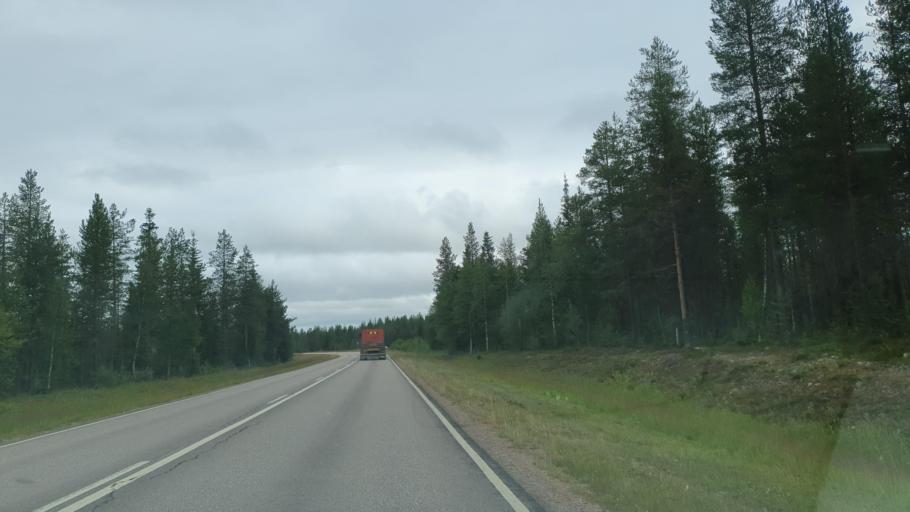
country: FI
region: Lapland
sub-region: Pohjois-Lappi
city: Sodankylae
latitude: 67.4215
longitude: 26.4450
